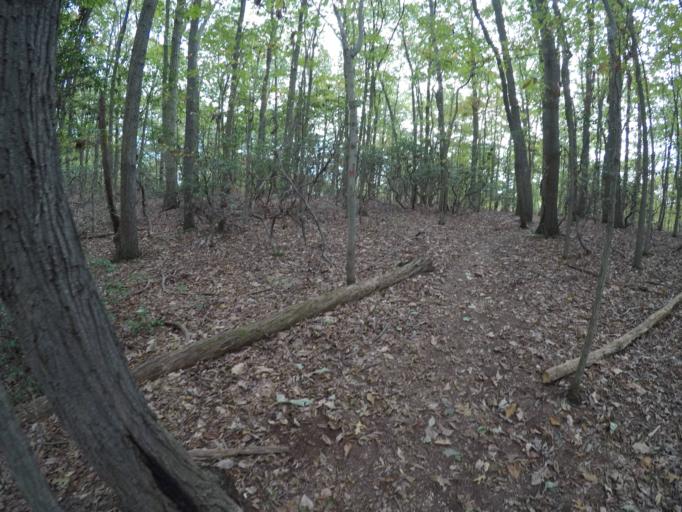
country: US
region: Maryland
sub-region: Harford County
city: Riverside
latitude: 39.4541
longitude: -76.2672
